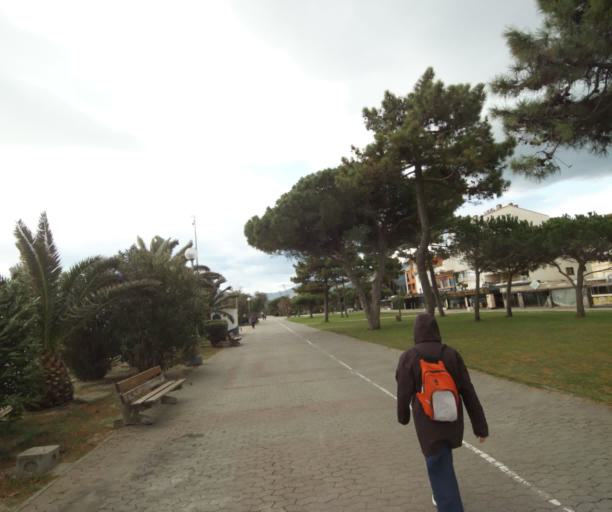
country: FR
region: Languedoc-Roussillon
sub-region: Departement des Pyrenees-Orientales
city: Argelers
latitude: 42.5522
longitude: 3.0481
